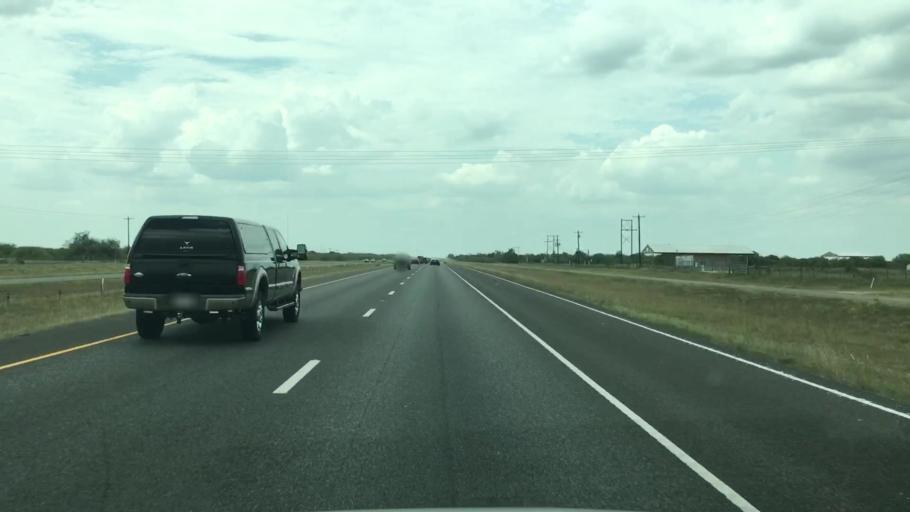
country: US
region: Texas
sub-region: Atascosa County
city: Pleasanton
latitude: 28.7982
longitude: -98.3408
